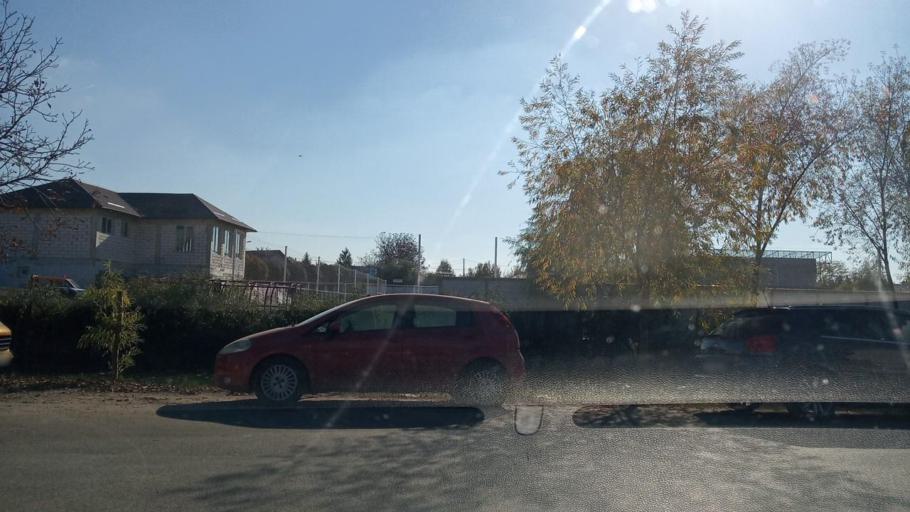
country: RO
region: Ilfov
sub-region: Comuna Tunari
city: Tunari
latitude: 44.5526
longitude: 26.1428
